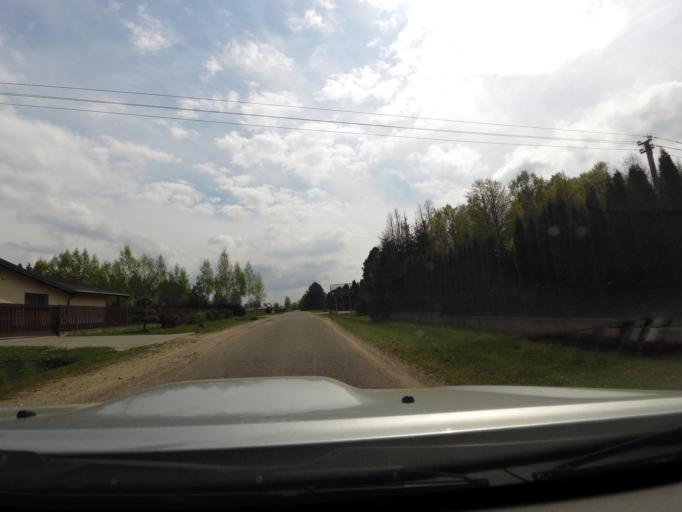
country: LT
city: Salcininkai
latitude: 54.4282
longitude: 25.3128
